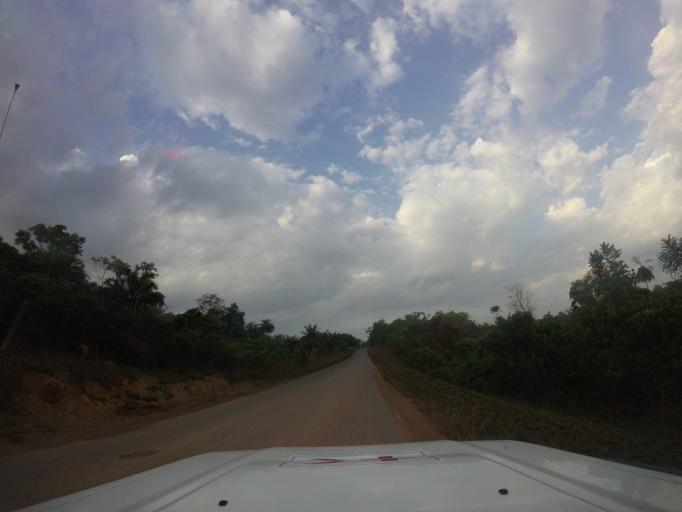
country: LR
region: Bomi
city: Tubmanburg
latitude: 6.7388
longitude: -10.8584
